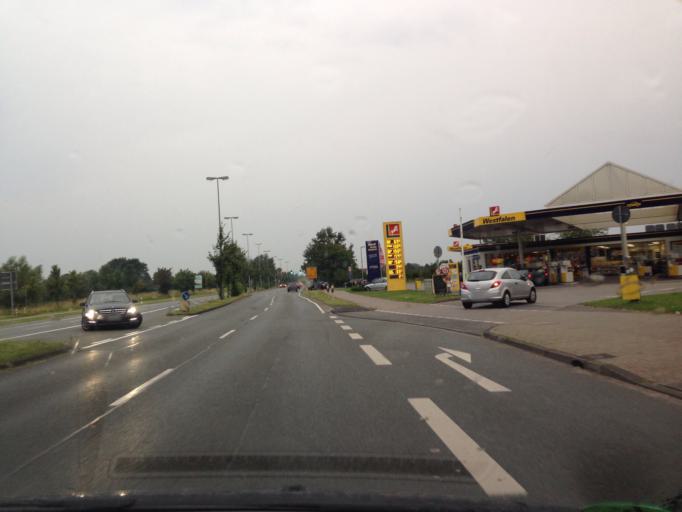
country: DE
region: North Rhine-Westphalia
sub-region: Regierungsbezirk Munster
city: Muenster
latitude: 51.9770
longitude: 7.6007
